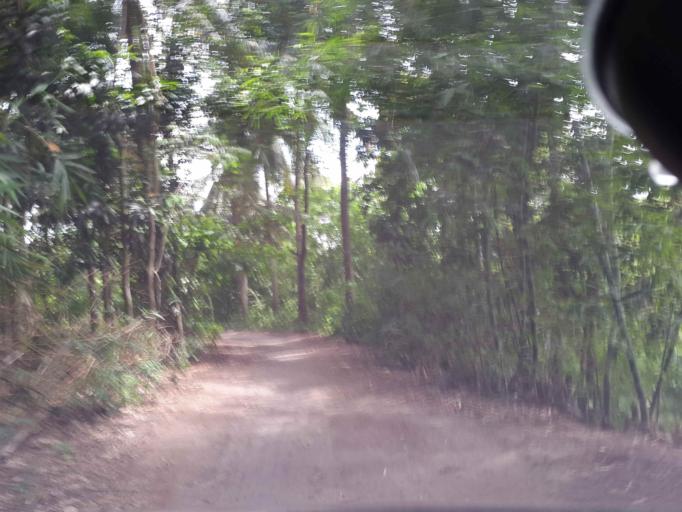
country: ID
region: West Nusa Tenggara
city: Jelateng Timur
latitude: -8.6949
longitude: 116.0912
